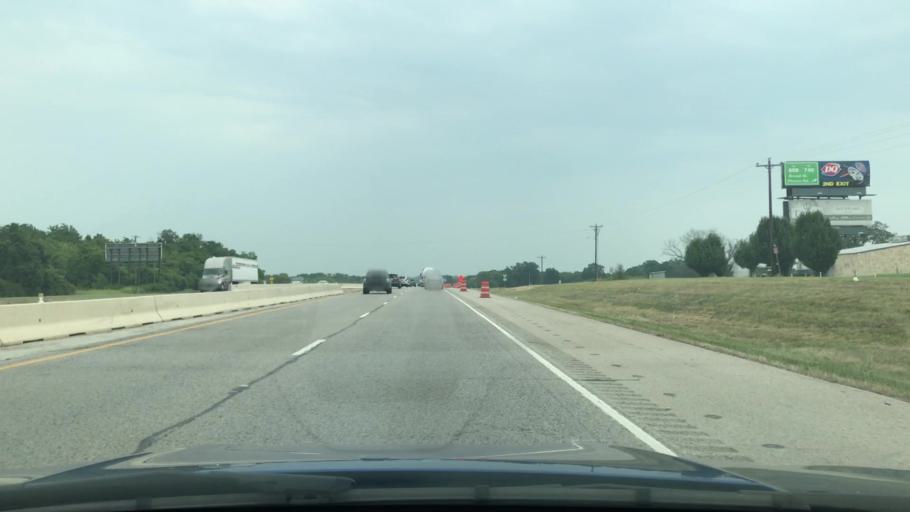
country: US
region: Texas
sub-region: Dallas County
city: Sunnyvale
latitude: 32.7766
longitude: -96.5145
